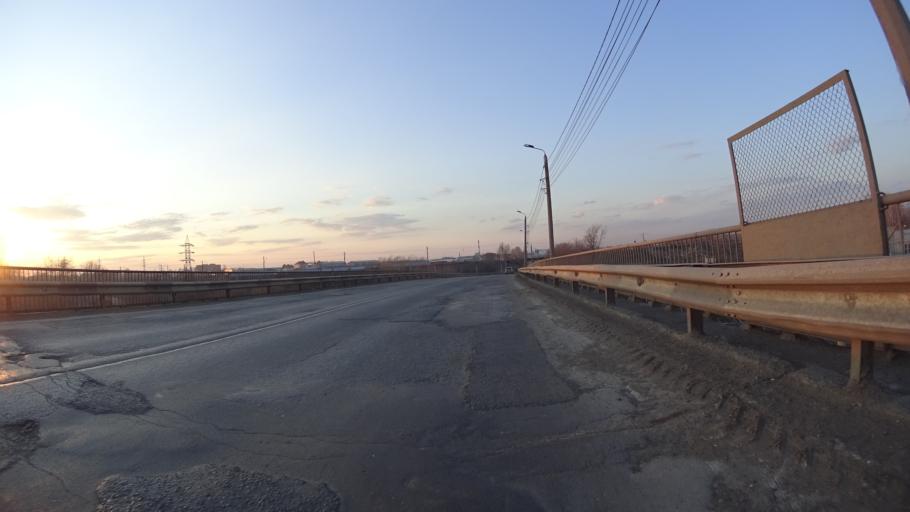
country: RU
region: Chelyabinsk
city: Novosineglazovskiy
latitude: 55.0815
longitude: 61.3883
